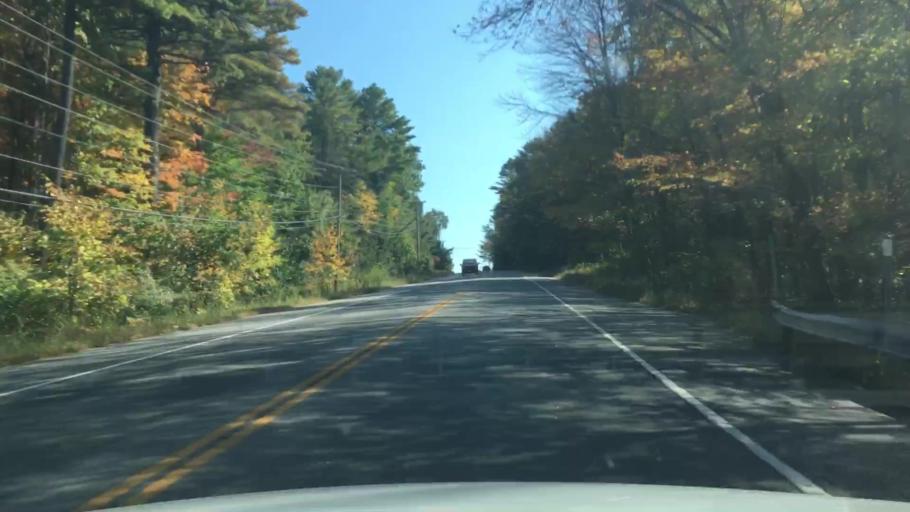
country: US
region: Maine
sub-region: Androscoggin County
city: Lisbon Falls
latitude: 43.9821
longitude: -70.0335
